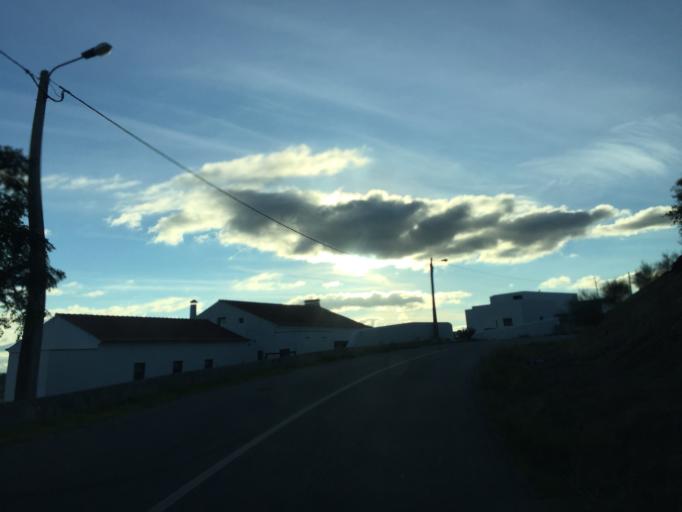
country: PT
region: Portalegre
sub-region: Alter do Chao
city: Alter do Chao
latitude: 39.2821
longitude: -7.6431
